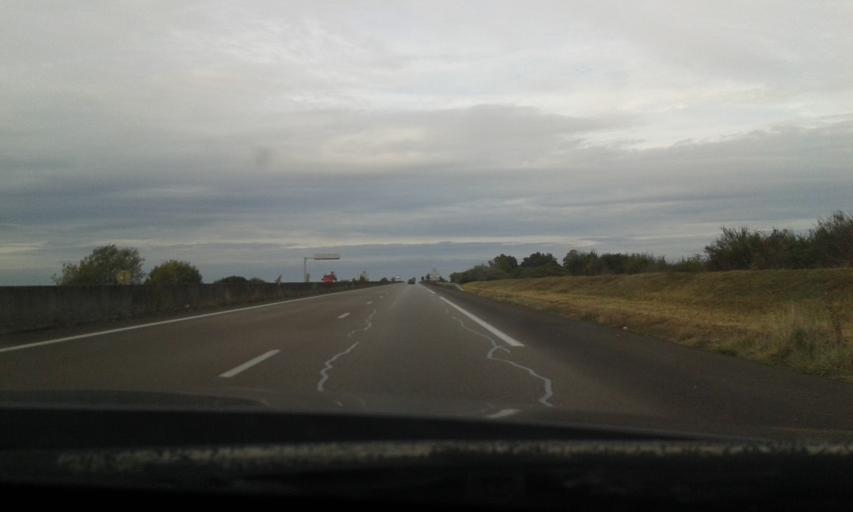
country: FR
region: Haute-Normandie
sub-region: Departement de l'Eure
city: La Madeleine-de-Nonancourt
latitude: 48.8554
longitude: 1.1791
